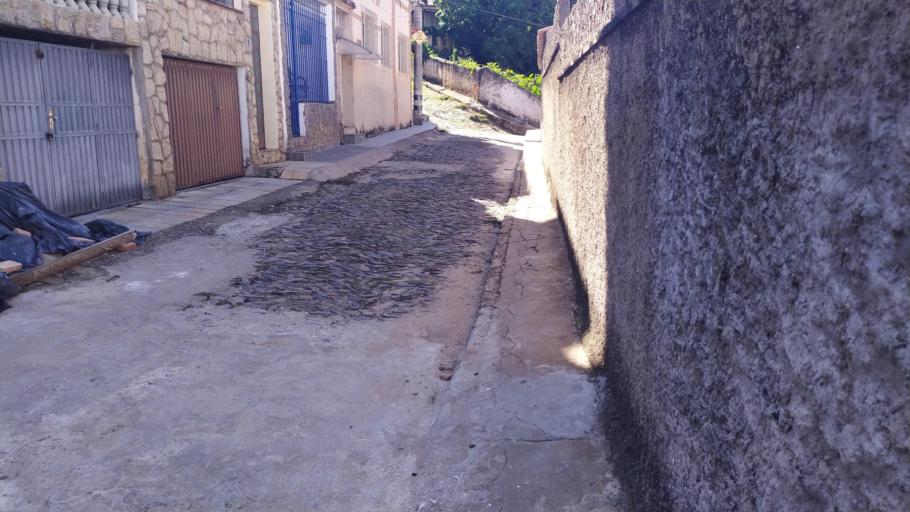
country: BR
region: Minas Gerais
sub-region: Sao Joao Del Rei
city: Sao Joao del Rei
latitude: -21.1328
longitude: -44.2619
